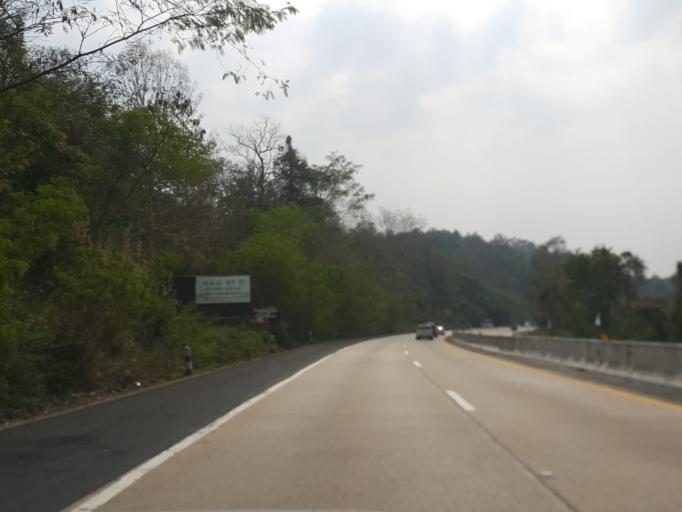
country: TH
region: Lampang
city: Hang Chat
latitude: 18.3450
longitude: 99.2456
